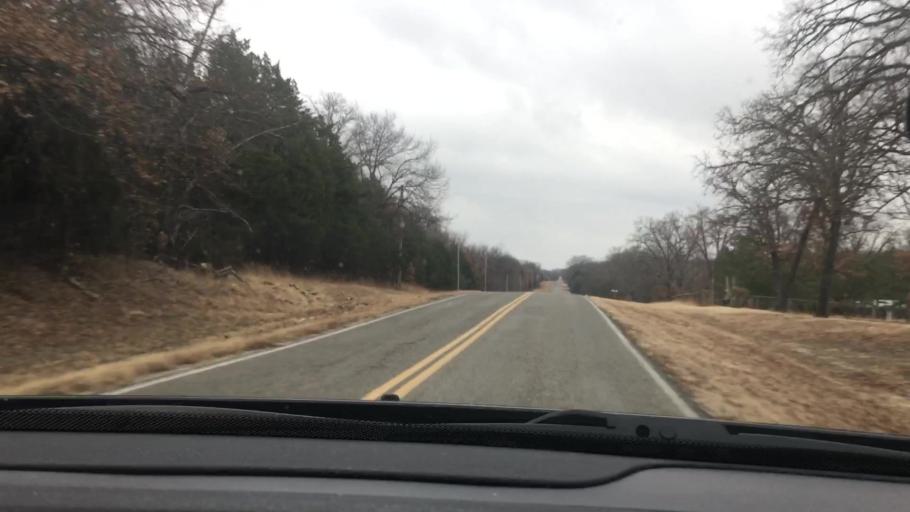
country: US
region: Oklahoma
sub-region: Johnston County
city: Tishomingo
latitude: 34.2087
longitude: -96.5999
